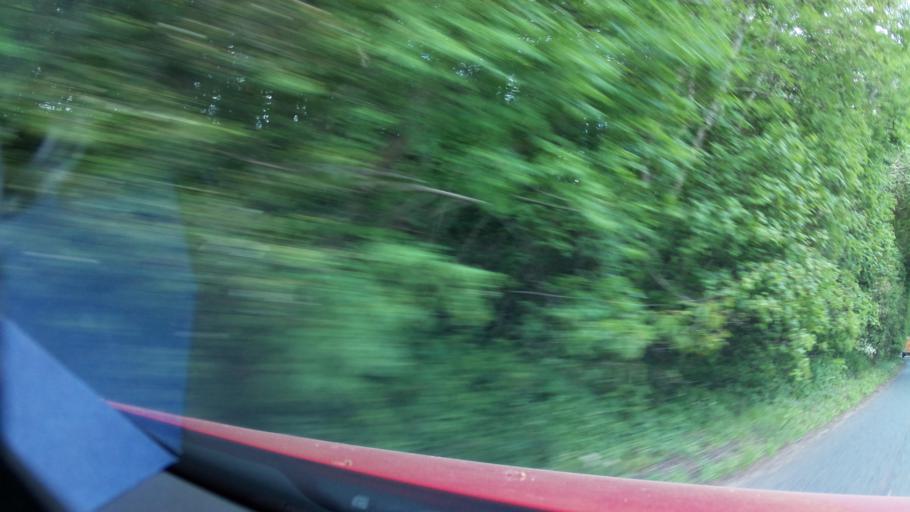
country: GB
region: England
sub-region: Worcestershire
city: Great Malvern
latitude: 52.1379
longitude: -2.3590
